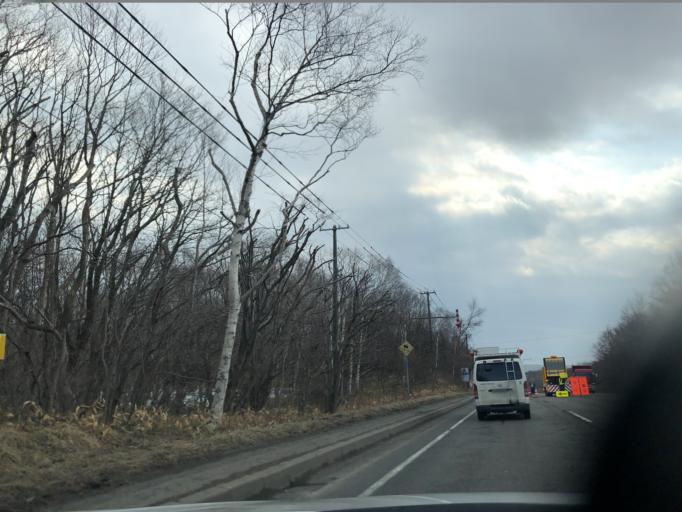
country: JP
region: Hokkaido
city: Chitose
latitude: 42.7720
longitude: 141.7071
